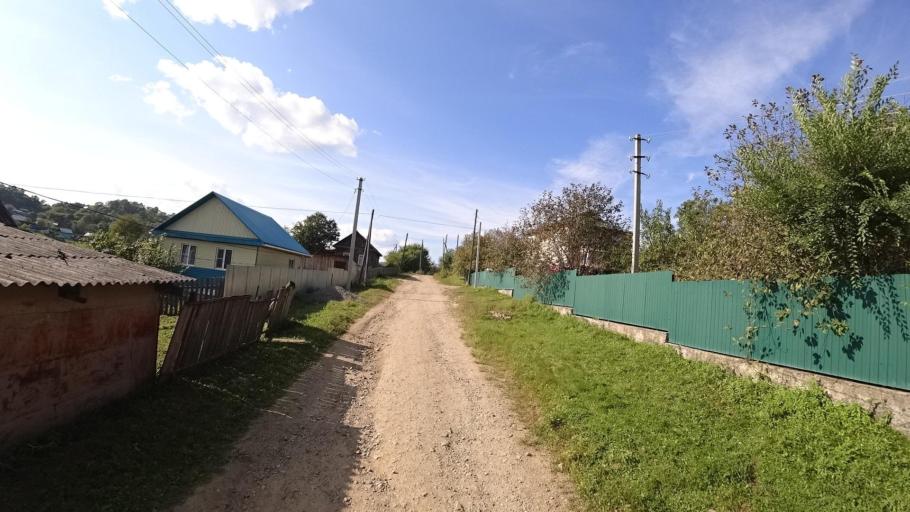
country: RU
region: Jewish Autonomous Oblast
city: Birakan
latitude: 48.9967
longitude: 131.7234
